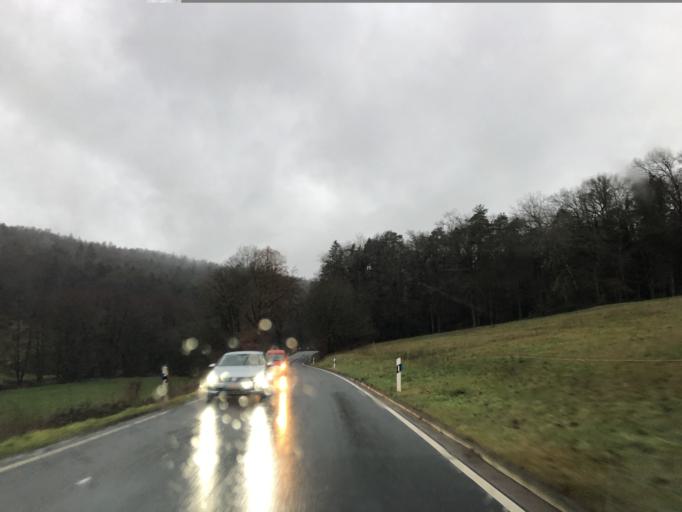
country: DE
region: Hesse
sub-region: Regierungsbezirk Darmstadt
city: Bad Konig
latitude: 49.7294
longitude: 9.0547
